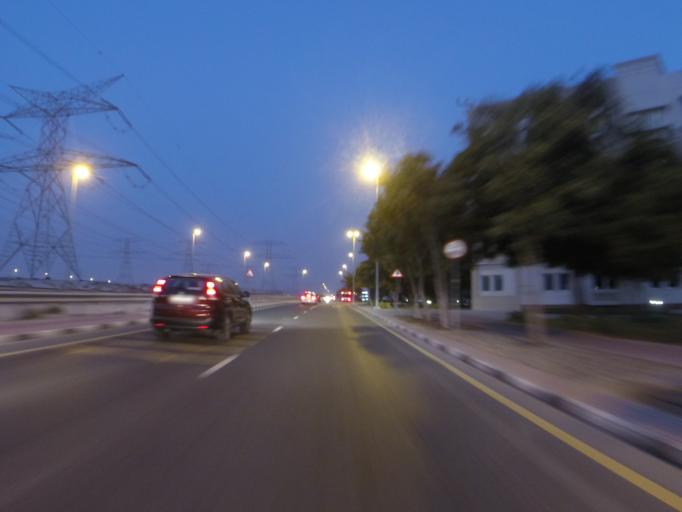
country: AE
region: Dubai
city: Dubai
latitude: 25.0497
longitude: 55.1354
